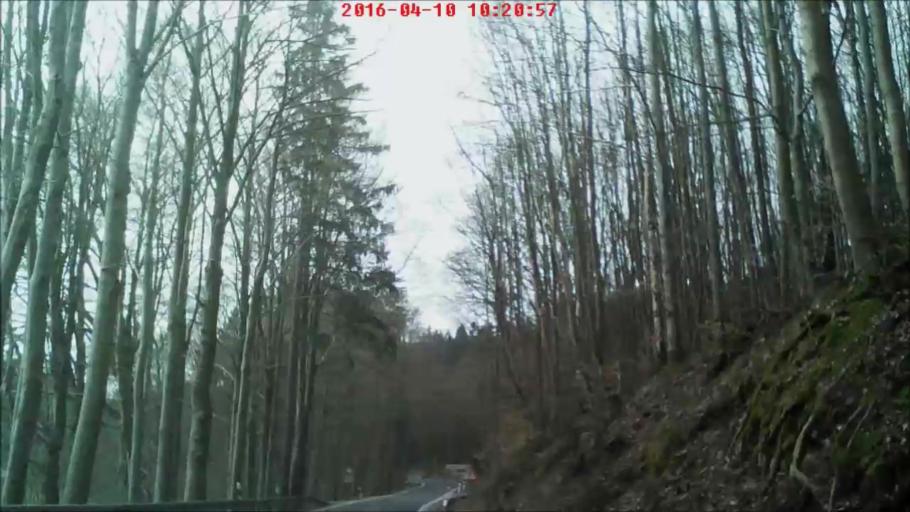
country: DE
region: Thuringia
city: Ilmenau
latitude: 50.6755
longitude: 10.9044
